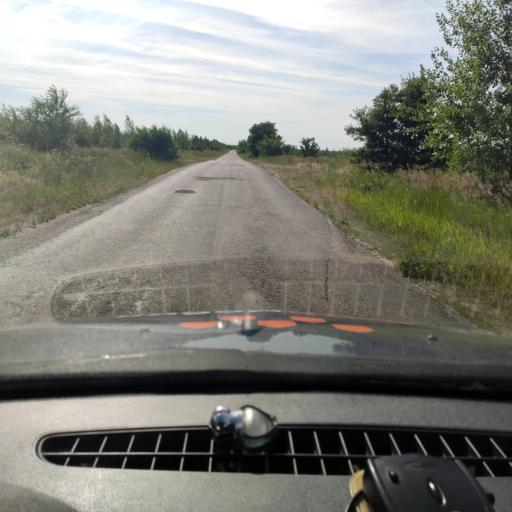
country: RU
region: Voronezj
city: Somovo
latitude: 51.7811
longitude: 39.3961
